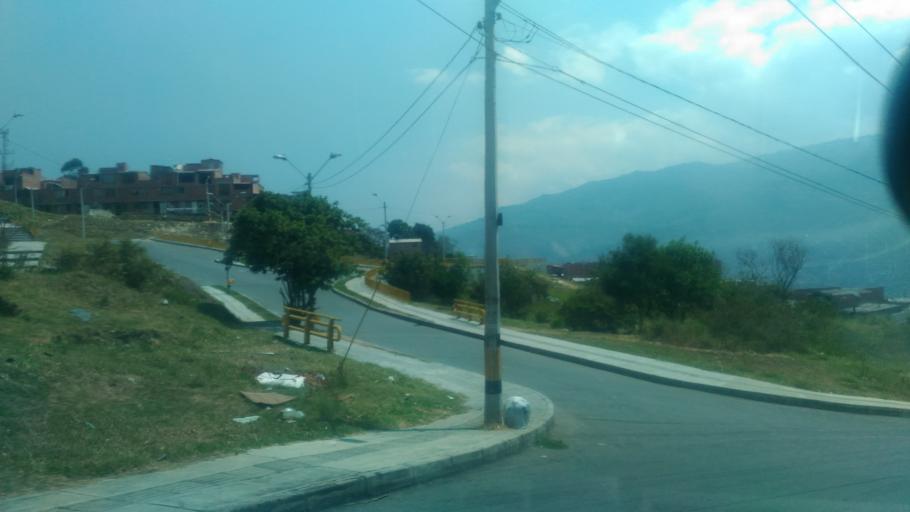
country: CO
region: Antioquia
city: Medellin
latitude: 6.2931
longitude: -75.5866
